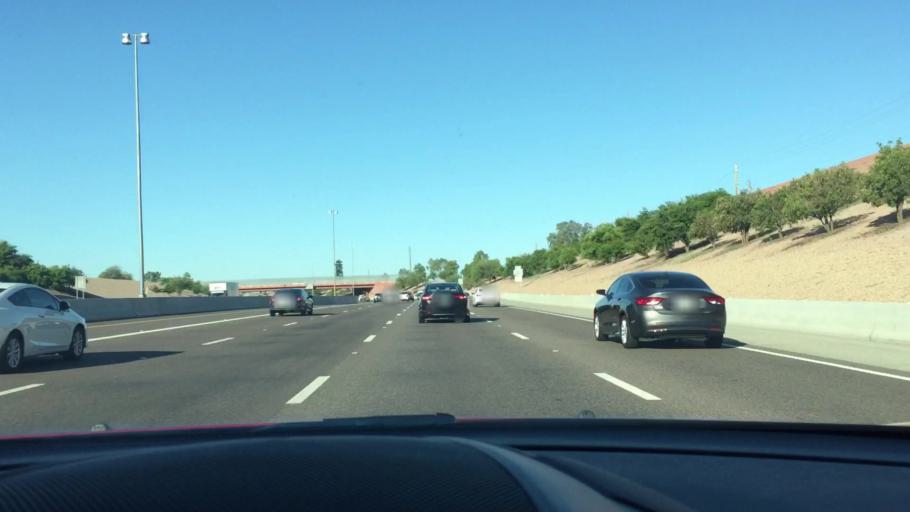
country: US
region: Arizona
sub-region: Maricopa County
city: Mesa
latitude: 33.4655
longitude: -111.8191
